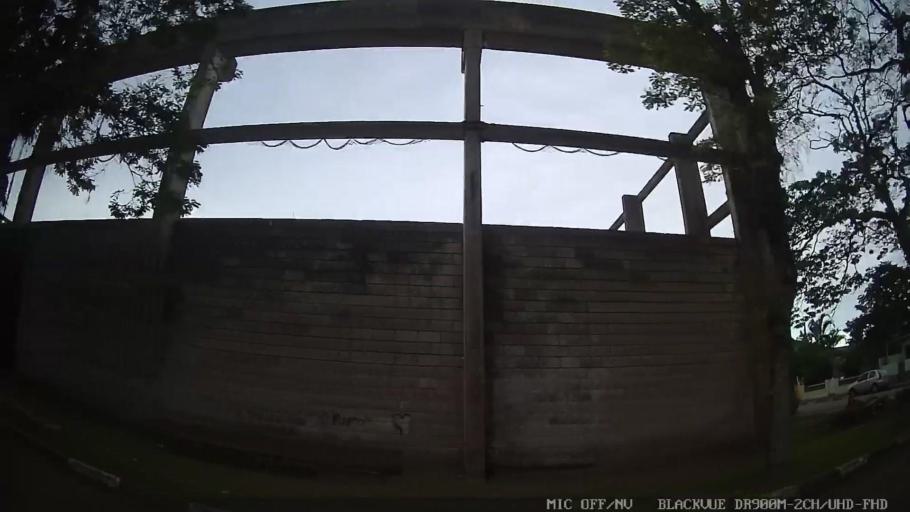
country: BR
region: Sao Paulo
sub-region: Iguape
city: Iguape
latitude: -24.7124
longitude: -47.5604
